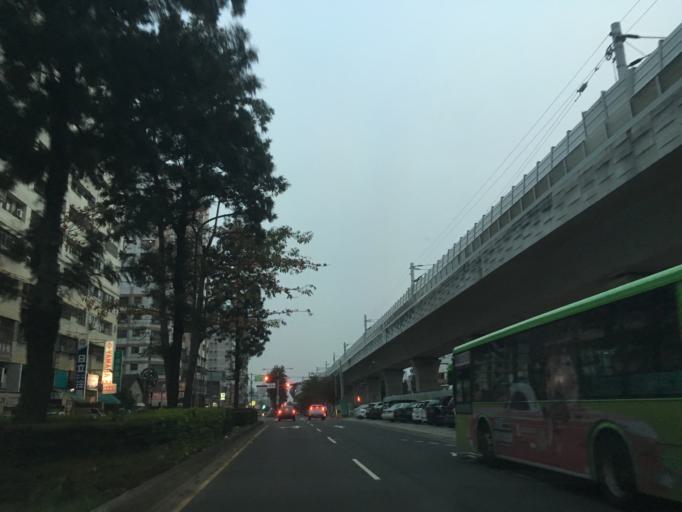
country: TW
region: Taiwan
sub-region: Taichung City
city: Taichung
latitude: 24.1687
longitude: 120.7007
